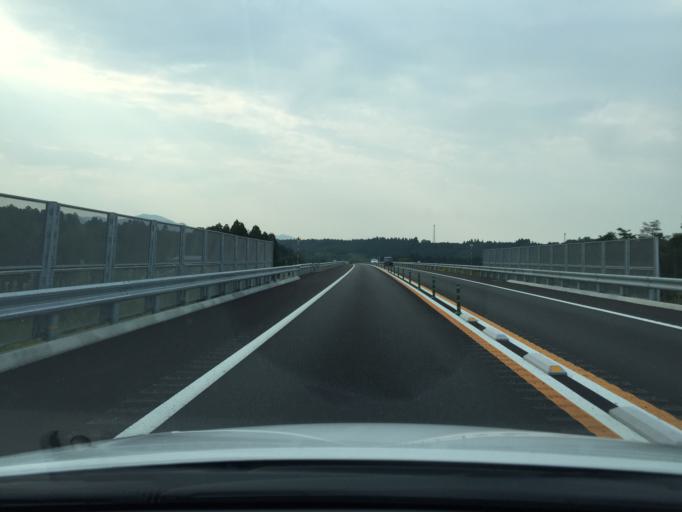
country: JP
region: Fukushima
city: Namie
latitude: 37.5796
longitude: 140.9384
